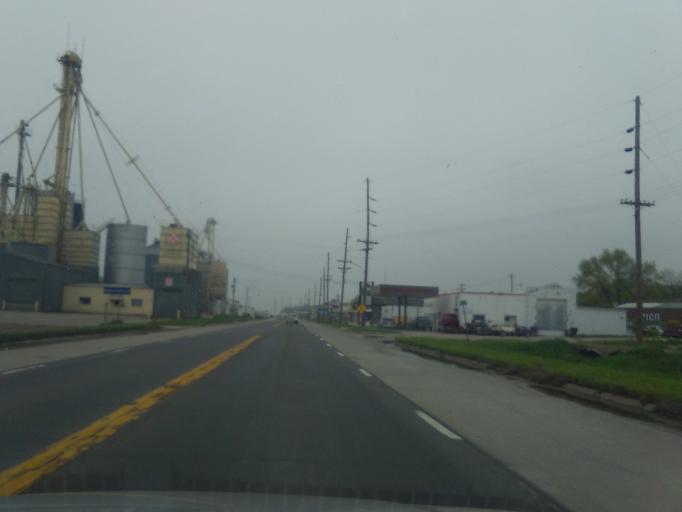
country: US
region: Nebraska
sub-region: Cuming County
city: Wisner
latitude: 41.9276
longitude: -96.8102
